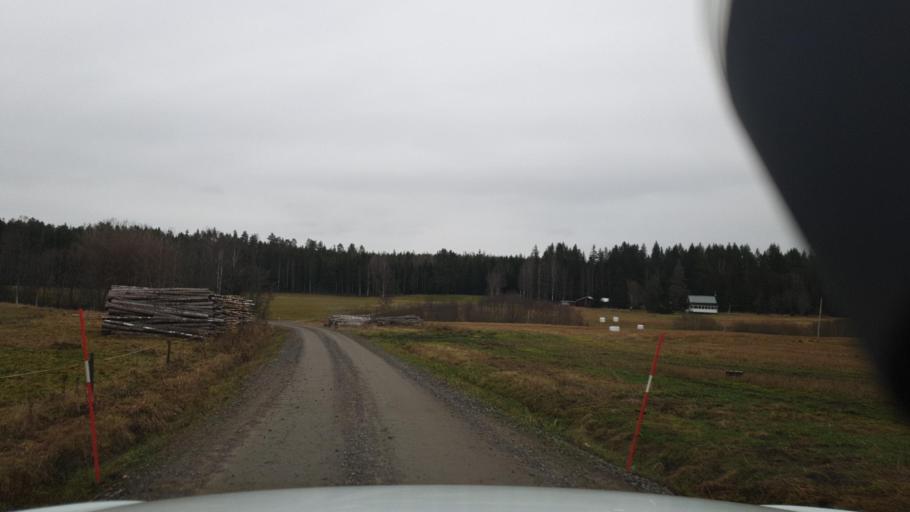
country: SE
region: Vaermland
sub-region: Karlstads Kommun
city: Edsvalla
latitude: 59.4783
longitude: 13.1320
